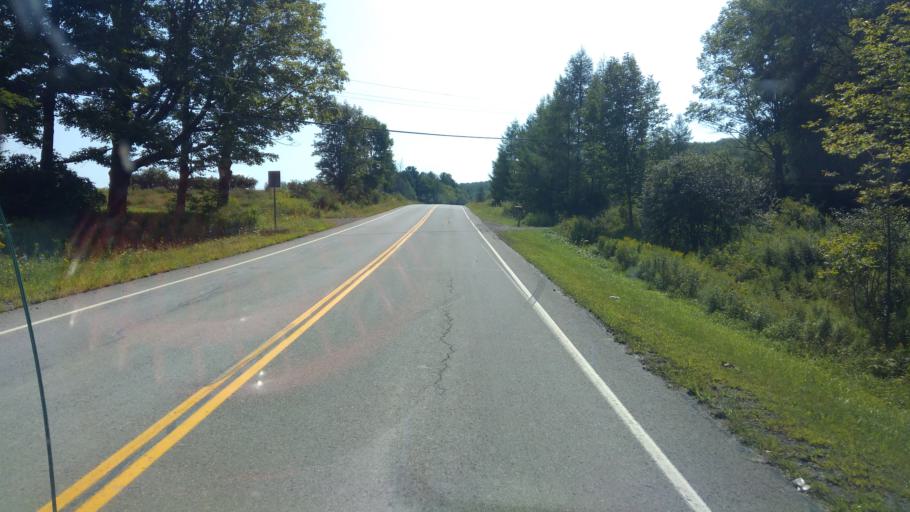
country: US
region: New York
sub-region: Allegany County
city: Belmont
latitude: 42.2969
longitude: -78.0095
